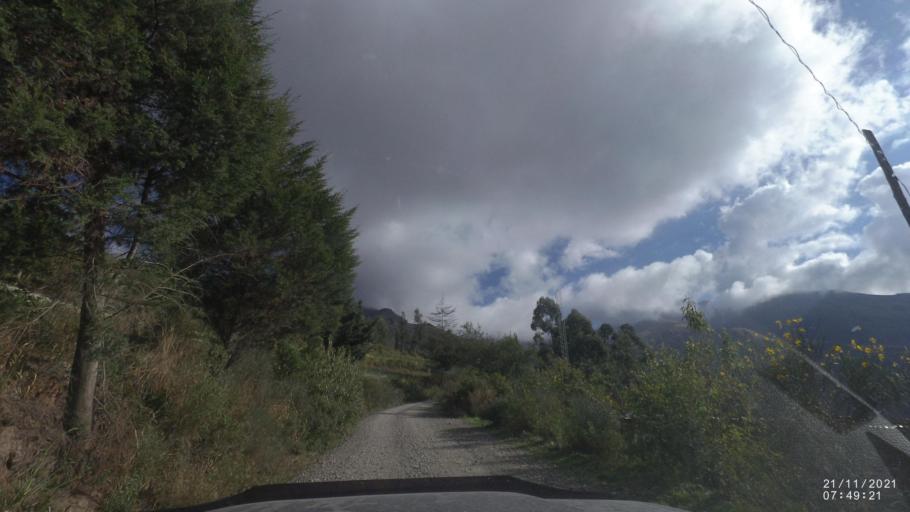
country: BO
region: Cochabamba
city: Cochabamba
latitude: -17.3098
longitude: -66.2140
